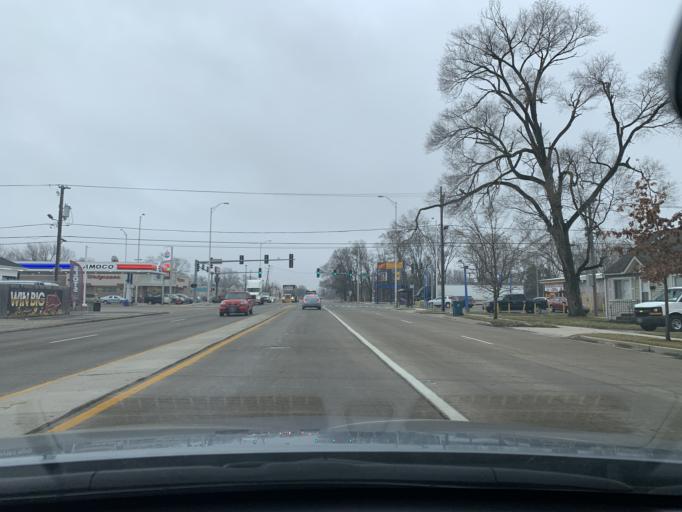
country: US
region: Illinois
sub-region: Cook County
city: Posen
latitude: 41.6268
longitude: -87.6984
